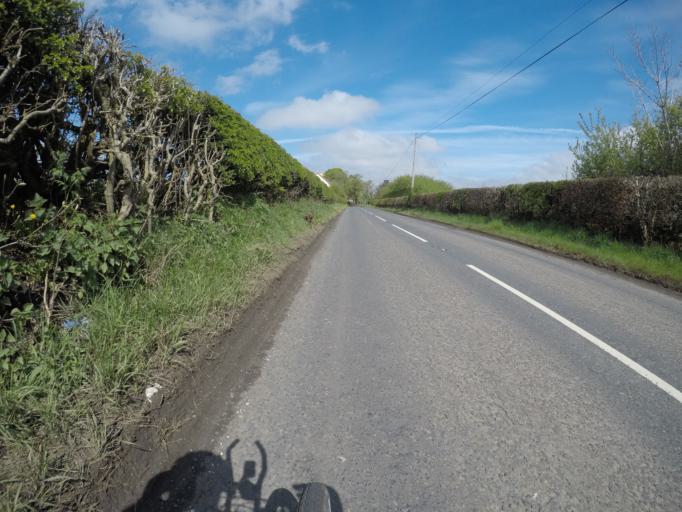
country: GB
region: Scotland
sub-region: East Ayrshire
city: Stewarton
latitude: 55.6926
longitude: -4.4927
